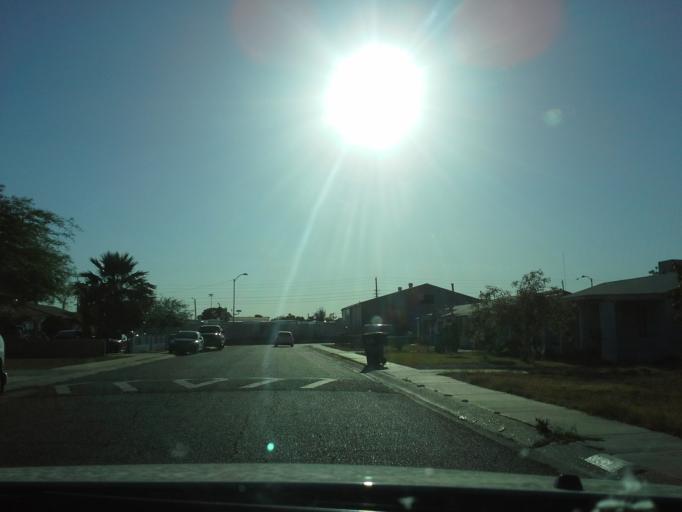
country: US
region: Arizona
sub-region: Maricopa County
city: Phoenix
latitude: 33.4317
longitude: -112.0980
